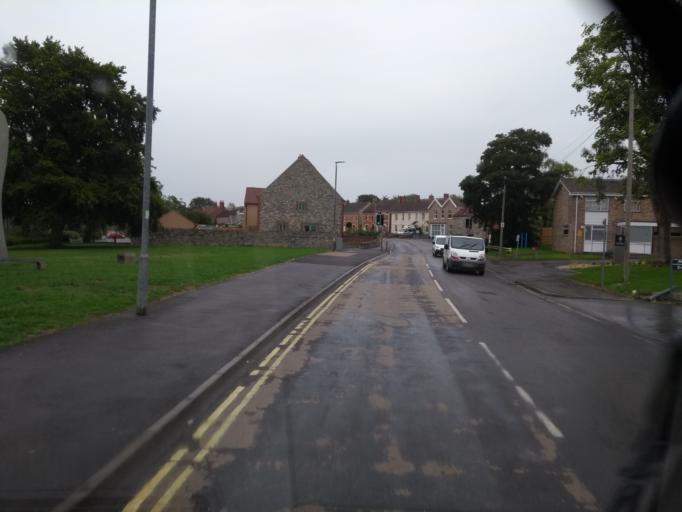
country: GB
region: England
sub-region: Somerset
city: Street
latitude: 51.1234
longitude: -2.7481
